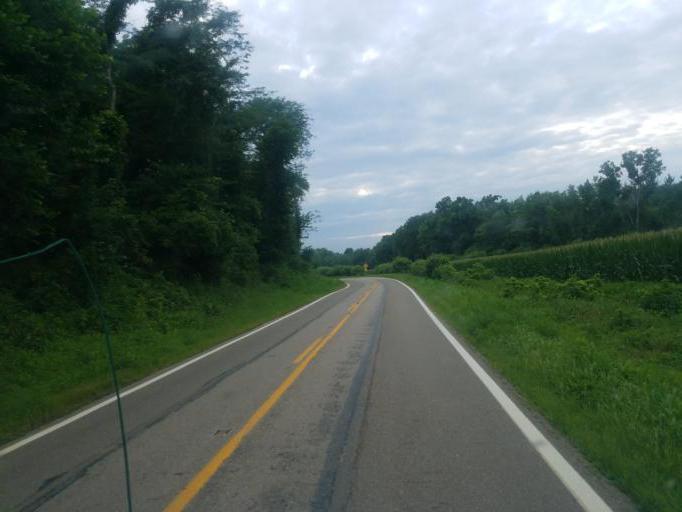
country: US
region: Ohio
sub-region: Knox County
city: Oak Hill
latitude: 40.3568
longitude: -82.1319
